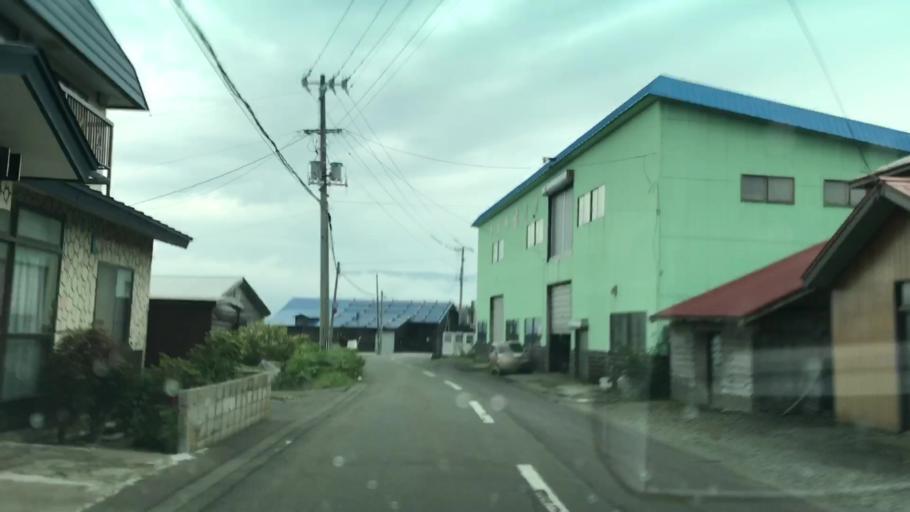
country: JP
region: Hokkaido
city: Iwanai
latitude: 42.7930
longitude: 140.2356
